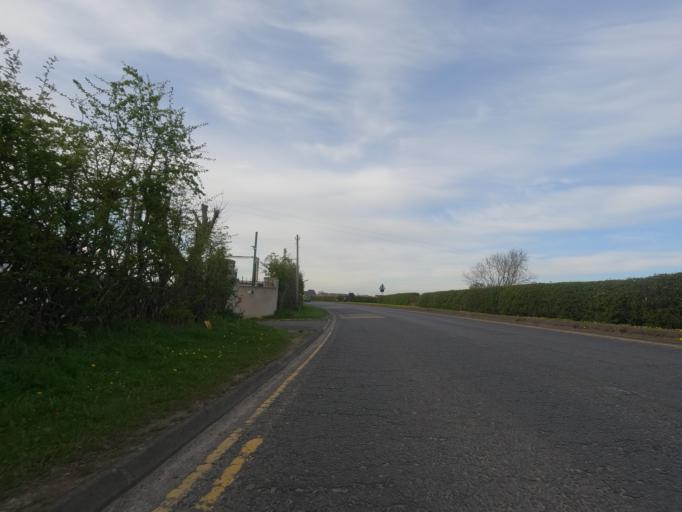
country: GB
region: England
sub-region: Newcastle upon Tyne
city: Dinnington
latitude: 55.0478
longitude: -1.6706
